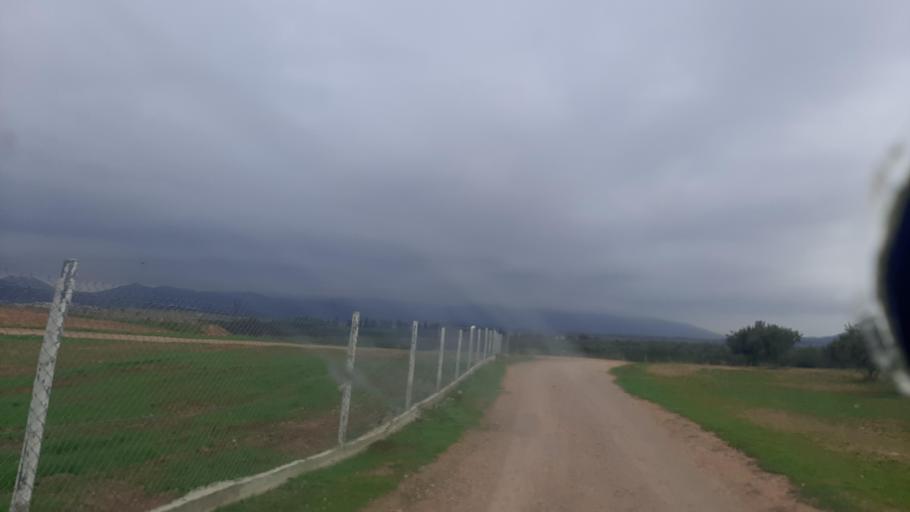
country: TN
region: Tunis
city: La Sebala du Mornag
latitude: 36.5672
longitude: 10.2955
